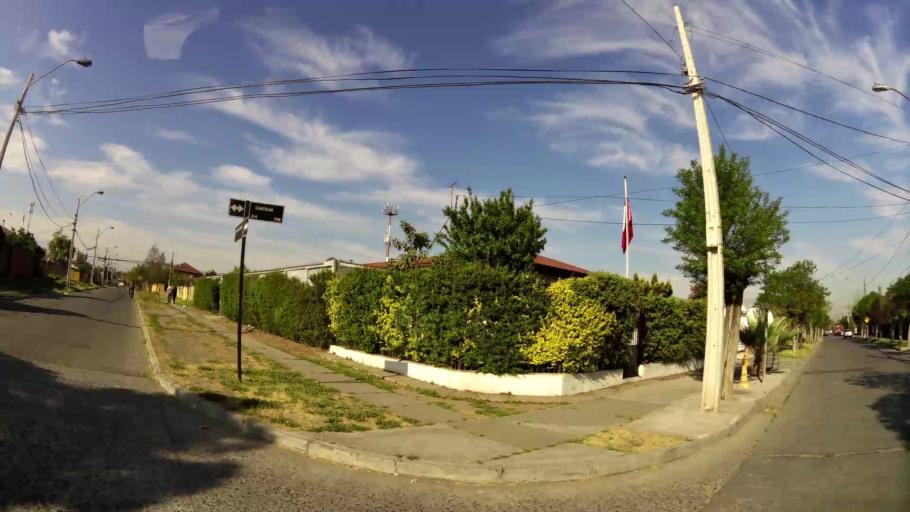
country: CL
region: Santiago Metropolitan
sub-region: Provincia de Cordillera
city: Puente Alto
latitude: -33.5644
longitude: -70.5878
